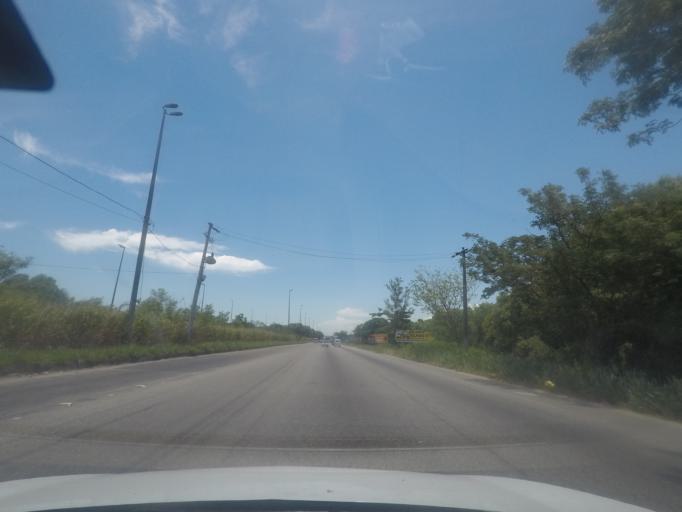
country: BR
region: Rio de Janeiro
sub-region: Itaguai
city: Itaguai
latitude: -22.8902
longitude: -43.6647
